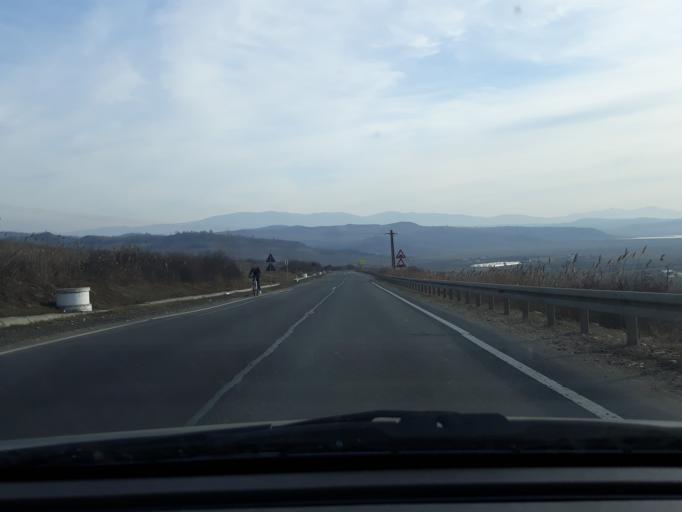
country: RO
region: Salaj
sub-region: Comuna Varsolt
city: Varsolt
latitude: 47.2144
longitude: 22.9285
